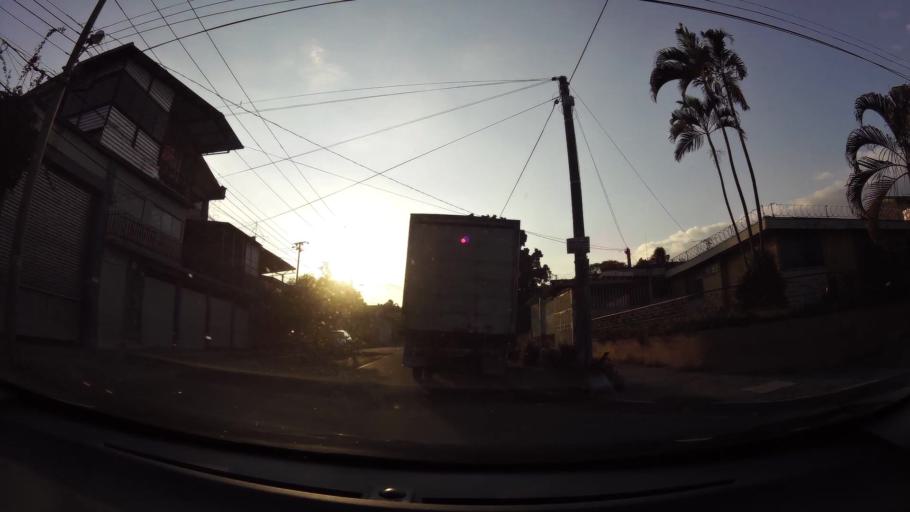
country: SV
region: San Salvador
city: Cuscatancingo
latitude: 13.7161
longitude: -89.1980
